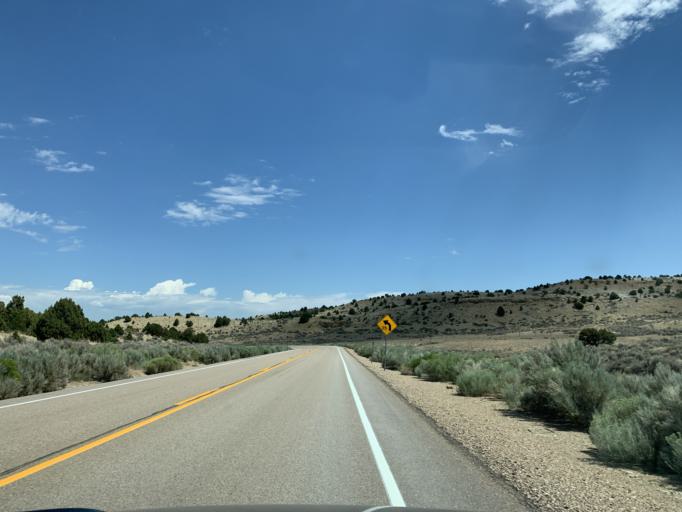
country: US
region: Utah
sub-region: Duchesne County
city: Duchesne
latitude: 39.8985
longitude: -110.2356
